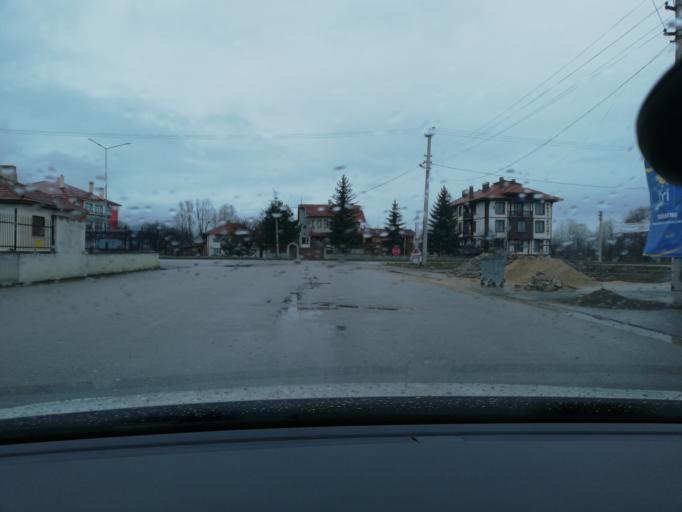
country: TR
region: Bolu
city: Bolu
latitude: 40.6938
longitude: 31.6201
